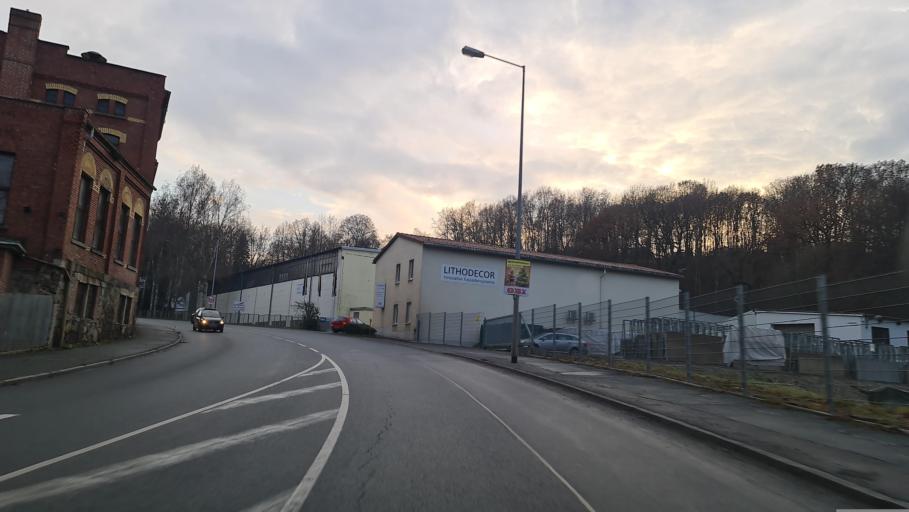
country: DE
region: Saxony
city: Netzschkau
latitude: 50.6207
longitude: 12.2534
